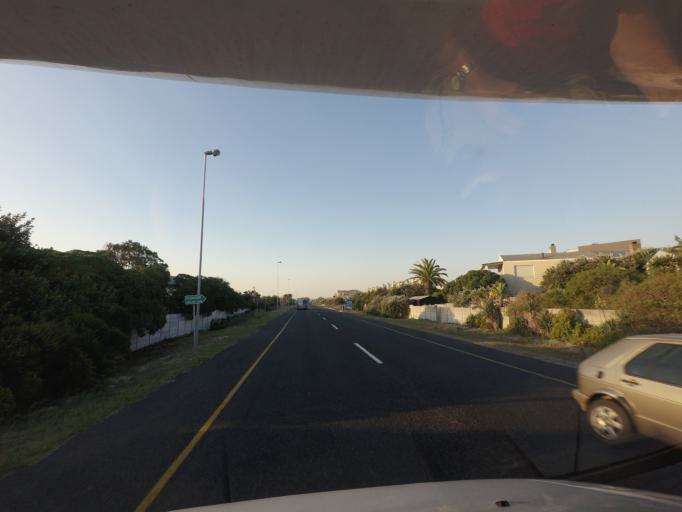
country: ZA
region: Western Cape
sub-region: City of Cape Town
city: Sunset Beach
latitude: -33.7187
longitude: 18.4461
